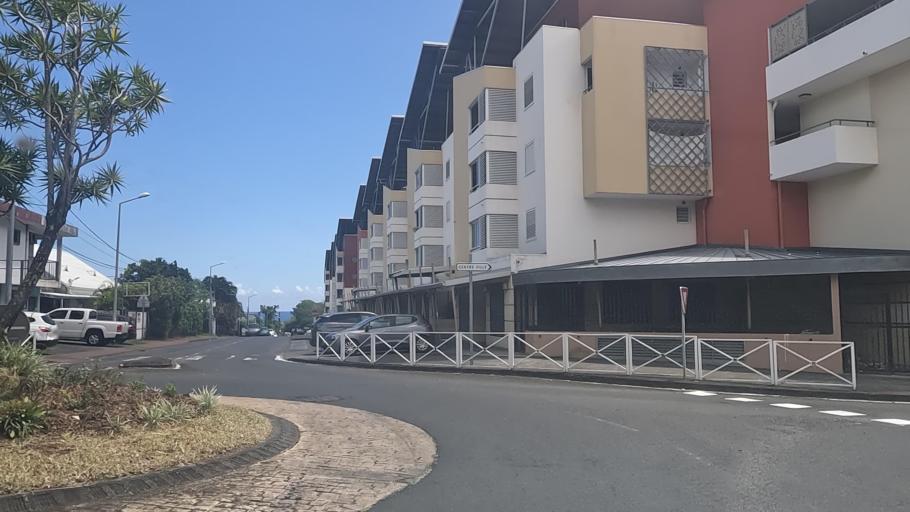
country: RE
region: Reunion
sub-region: Reunion
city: Saint-Benoit
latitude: -21.0328
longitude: 55.7084
